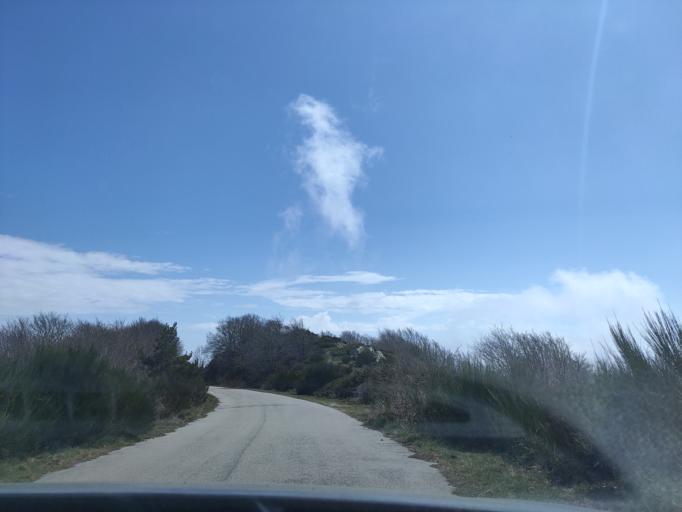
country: ES
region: Catalonia
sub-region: Provincia de Barcelona
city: Fogars de Montclus
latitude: 41.7671
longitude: 2.4516
